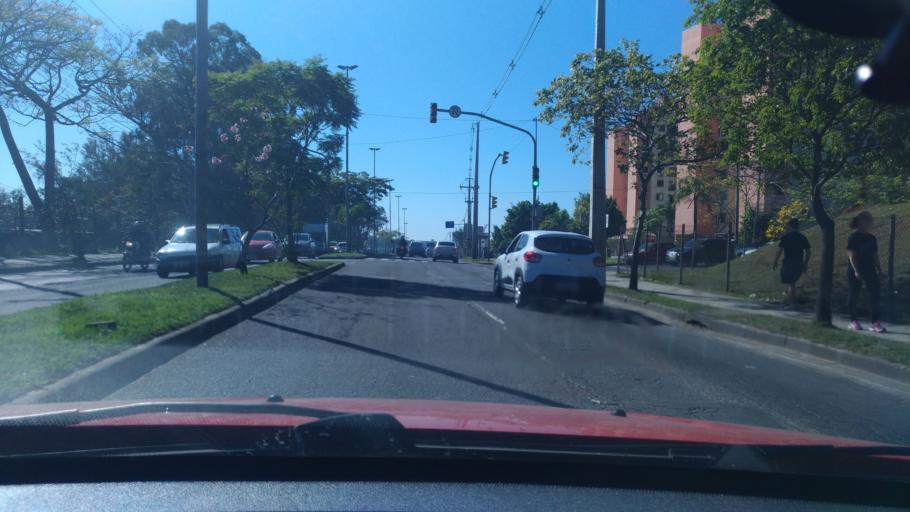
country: BR
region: Rio Grande do Sul
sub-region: Porto Alegre
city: Porto Alegre
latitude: -30.0434
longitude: -51.1390
